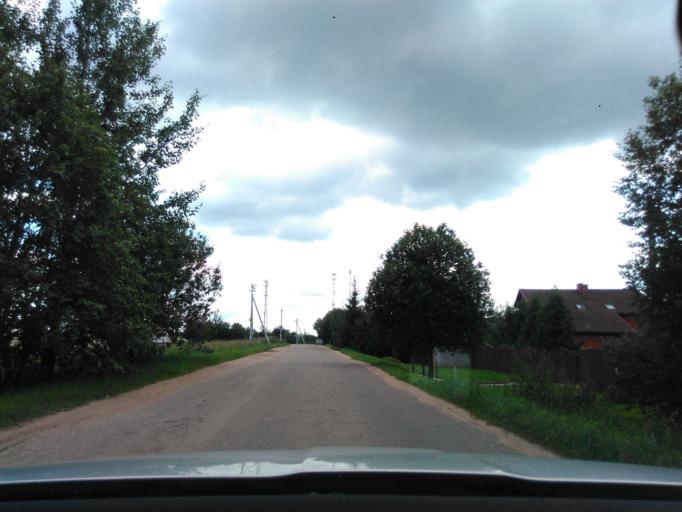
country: RU
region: Moskovskaya
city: Mendeleyevo
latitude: 56.1010
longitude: 37.2700
